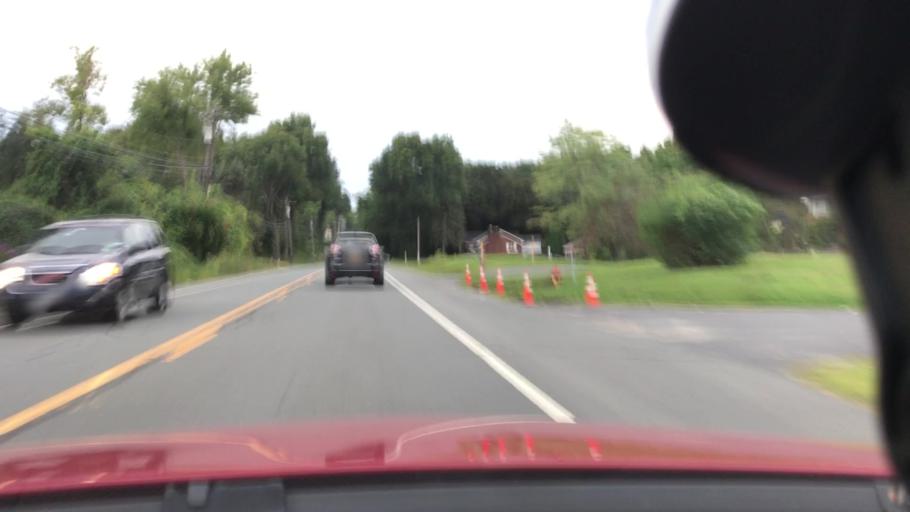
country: US
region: New York
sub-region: Albany County
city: Menands
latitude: 42.6874
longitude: -73.6880
